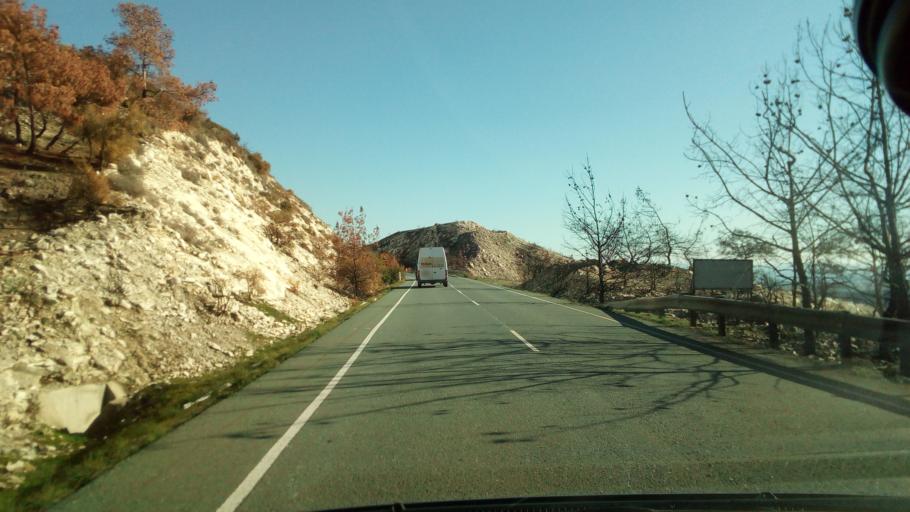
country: CY
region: Larnaka
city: Kofinou
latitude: 34.8138
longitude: 33.3095
